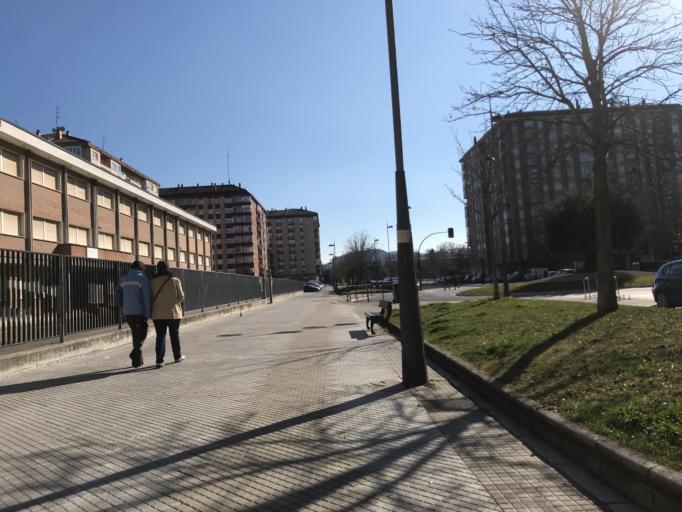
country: ES
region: Basque Country
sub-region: Provincia de Alava
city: Gasteiz / Vitoria
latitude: 42.8444
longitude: -2.6581
